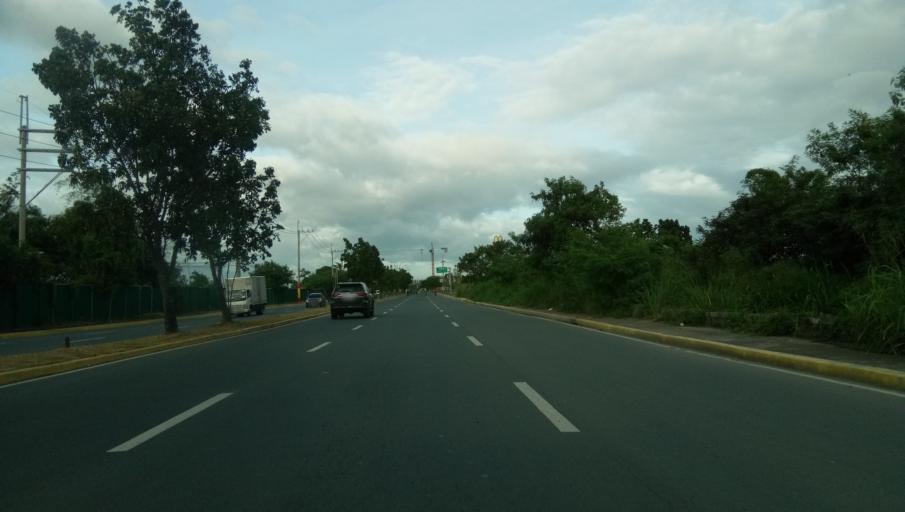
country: PH
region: Calabarzon
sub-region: Province of Cavite
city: Dasmarinas
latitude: 14.3794
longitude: 120.9551
